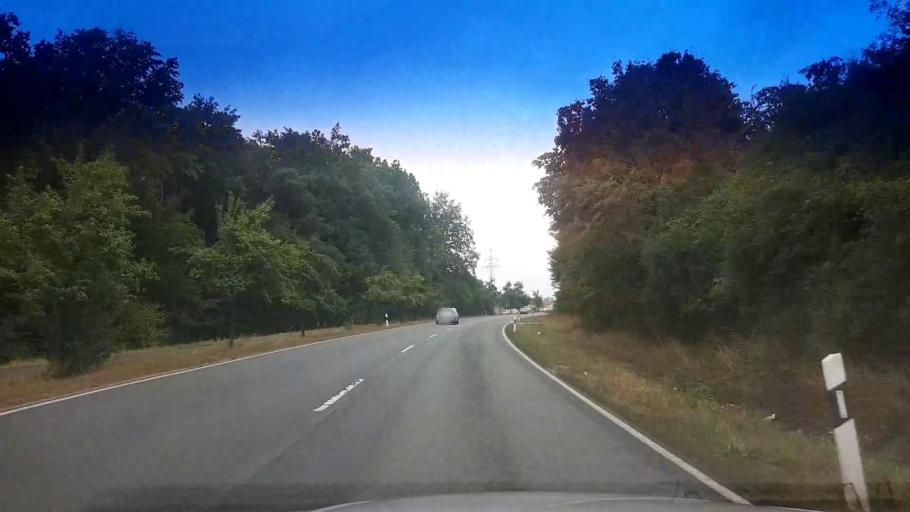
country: DE
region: Bavaria
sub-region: Upper Franconia
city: Forchheim
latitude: 49.7093
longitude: 11.0422
